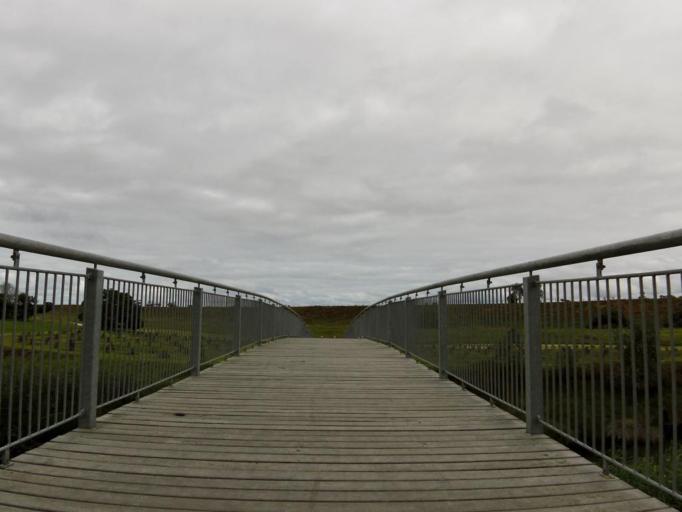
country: AU
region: Victoria
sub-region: Wyndham
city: Werribee
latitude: -37.9344
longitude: 144.6616
